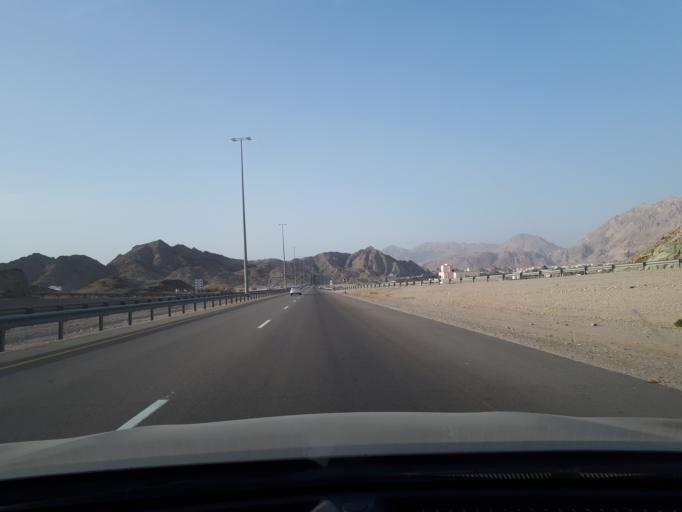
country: OM
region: Muhafazat Masqat
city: Bawshar
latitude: 23.4153
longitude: 58.4969
